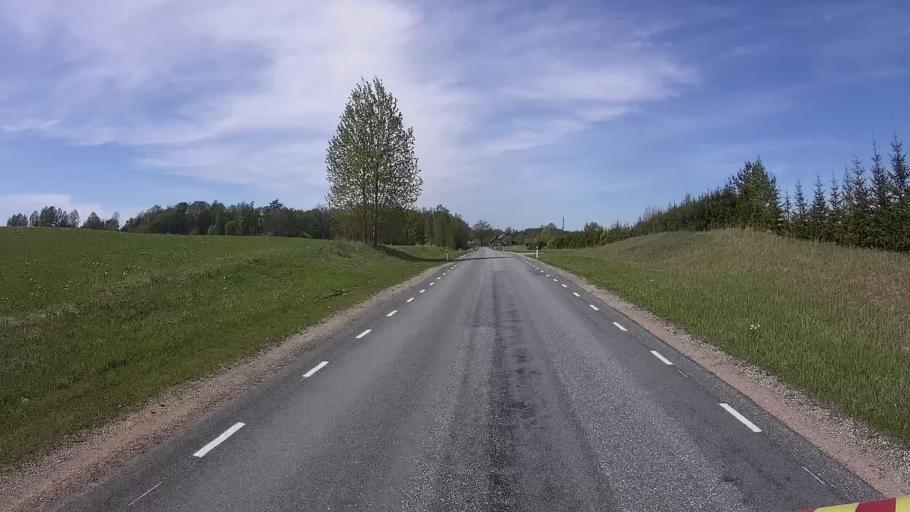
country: EE
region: Valgamaa
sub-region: Valga linn
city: Valga
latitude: 57.6506
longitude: 26.3055
